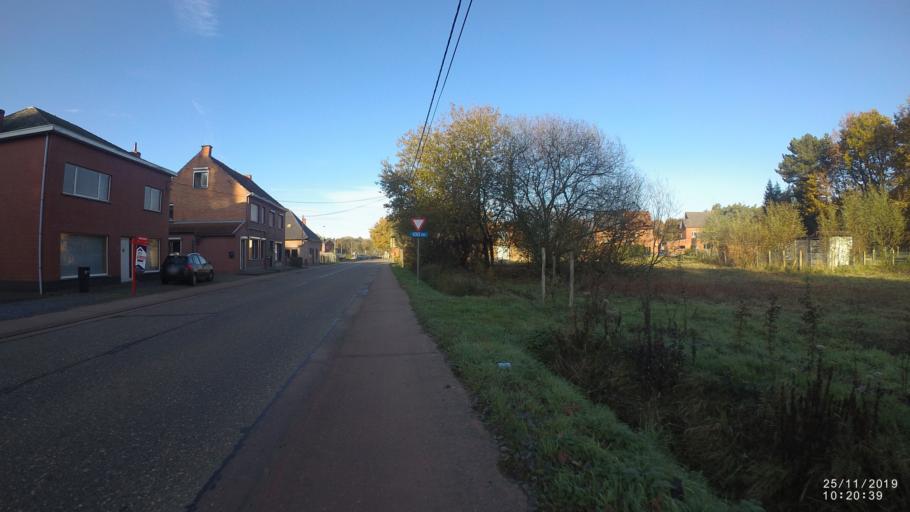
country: BE
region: Flanders
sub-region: Provincie Vlaams-Brabant
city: Scherpenheuvel-Zichem
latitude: 51.0150
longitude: 5.0051
